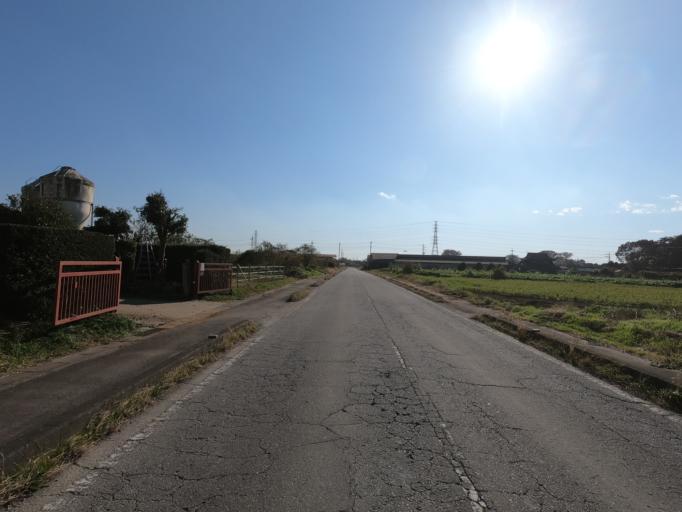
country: JP
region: Ibaraki
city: Tsukuba
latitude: 36.1384
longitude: 140.1495
